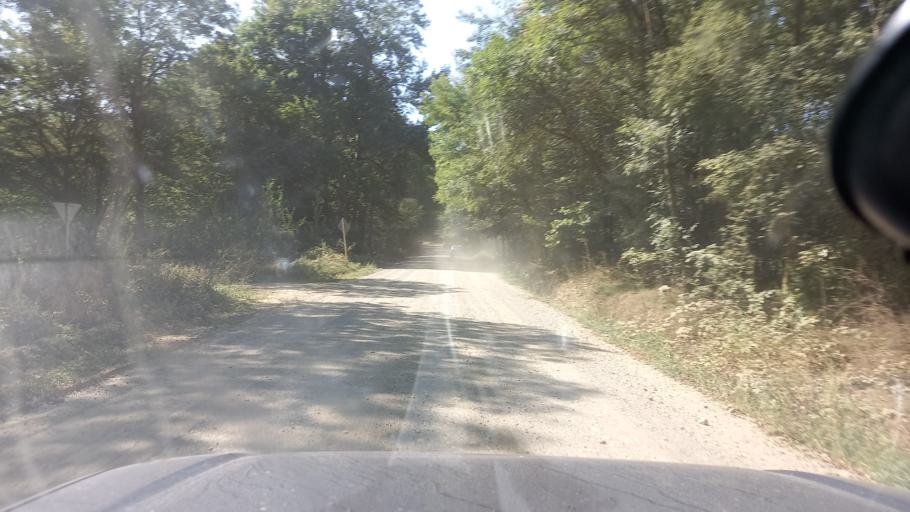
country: RU
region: Krasnodarskiy
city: Azovskaya
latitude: 44.6940
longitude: 38.6414
